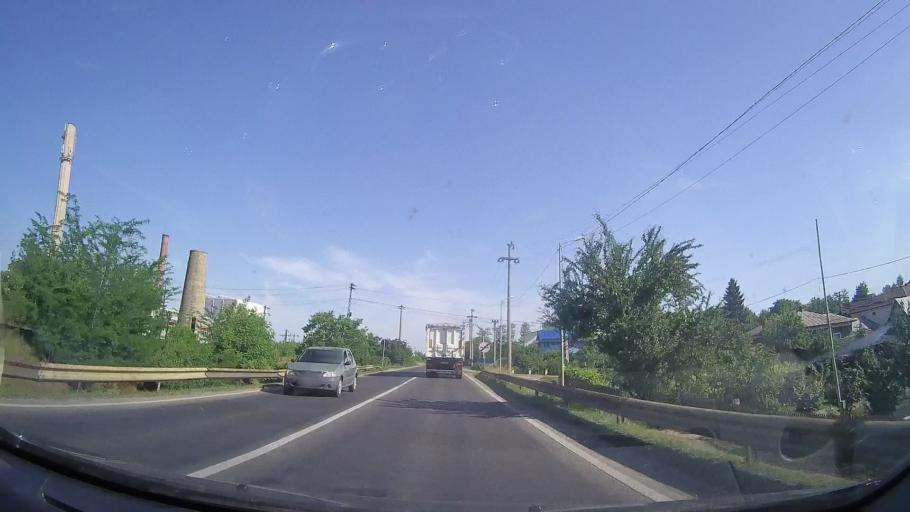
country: RO
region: Prahova
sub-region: Comuna Blejoiu
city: Blejoi
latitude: 44.9919
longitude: 26.0133
